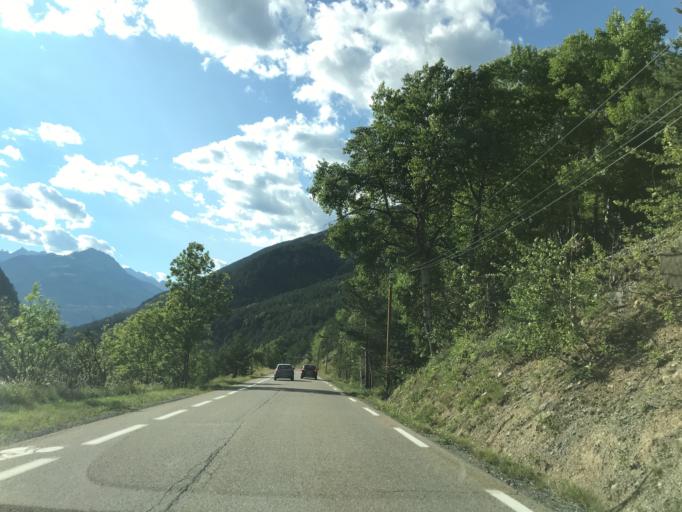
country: FR
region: Provence-Alpes-Cote d'Azur
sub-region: Departement des Hautes-Alpes
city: Briancon
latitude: 44.8746
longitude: 6.6927
